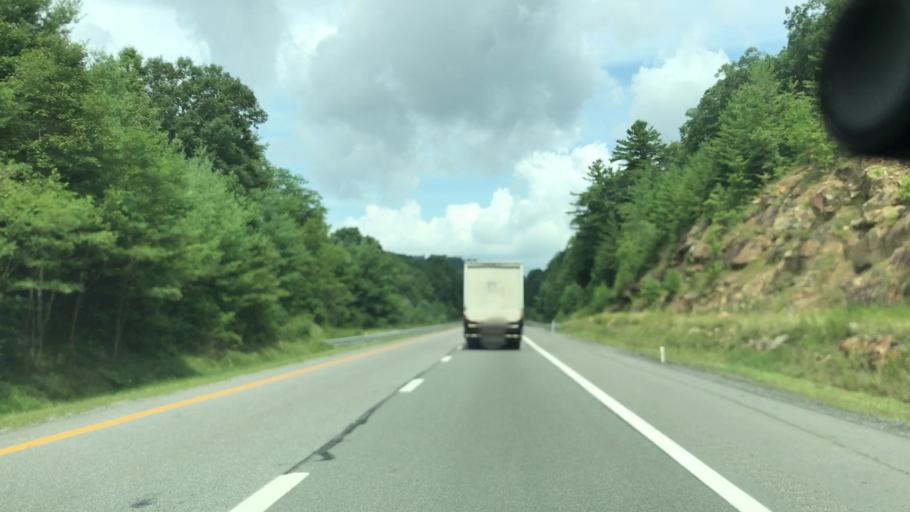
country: US
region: West Virginia
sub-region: Raleigh County
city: Shady Spring
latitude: 37.7010
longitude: -81.1403
